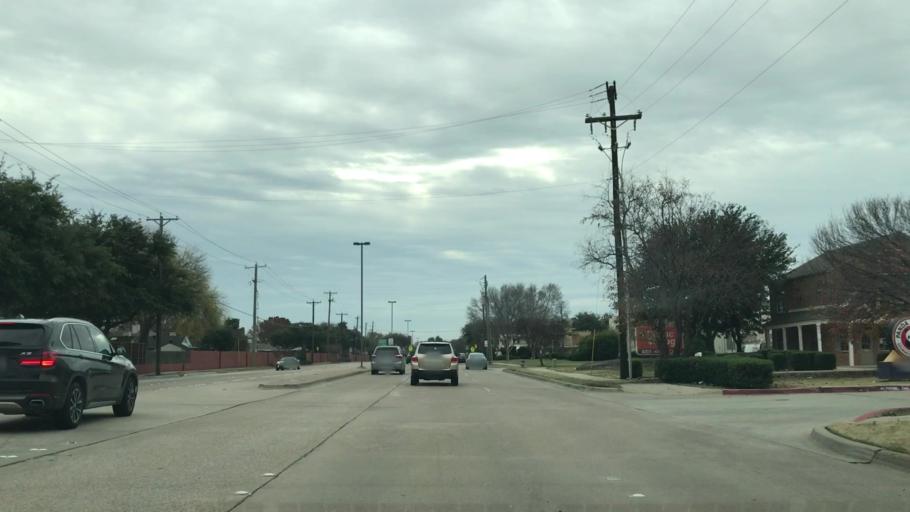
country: US
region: Texas
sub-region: Denton County
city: The Colony
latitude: 33.0231
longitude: -96.8850
